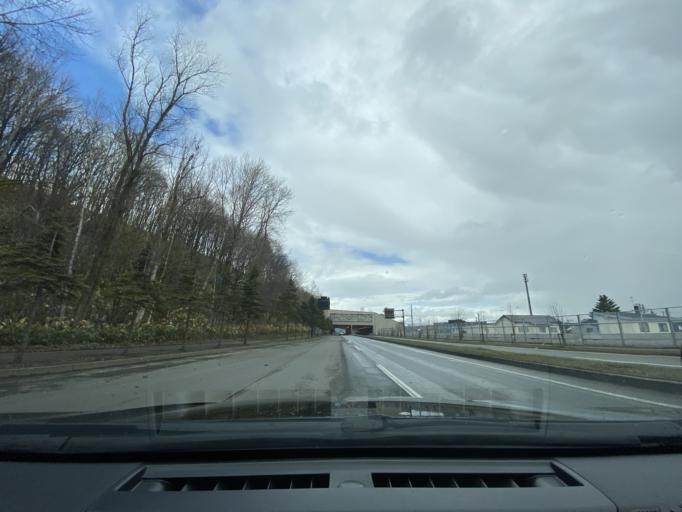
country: JP
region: Hokkaido
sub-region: Asahikawa-shi
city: Asahikawa
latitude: 43.8076
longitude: 142.3573
